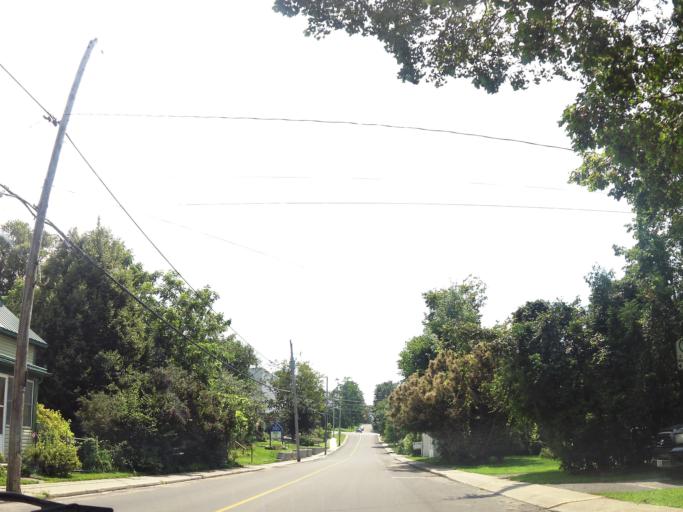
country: CA
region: Ontario
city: Kingston
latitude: 44.4086
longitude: -76.5966
